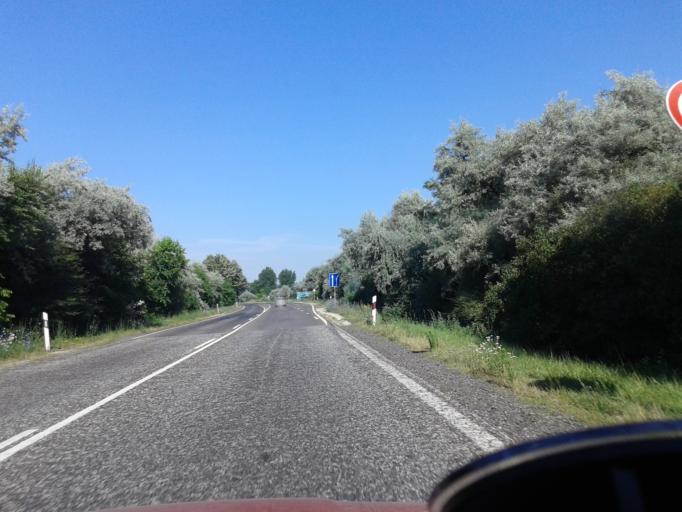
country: HU
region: Pest
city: Biatorbagy
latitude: 47.4909
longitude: 18.8191
